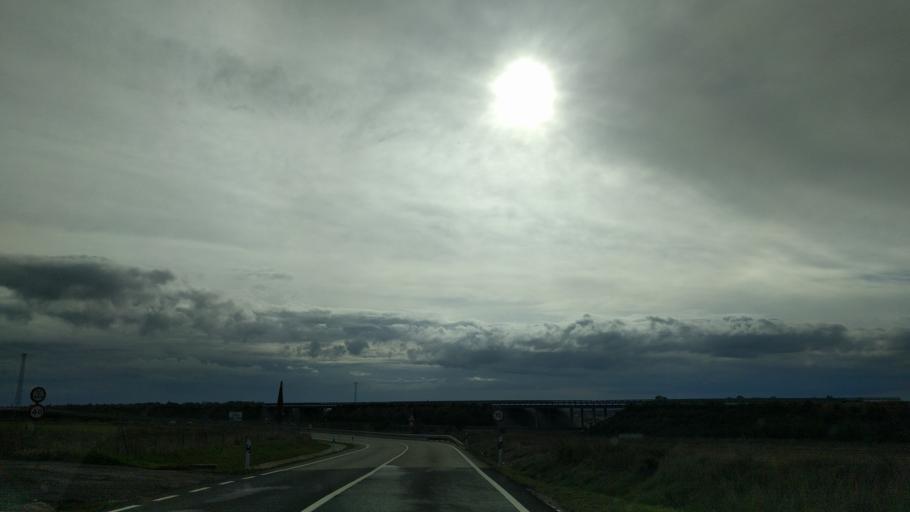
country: ES
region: Aragon
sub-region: Provincia de Huesca
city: Sietamo
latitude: 42.1200
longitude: -0.2922
